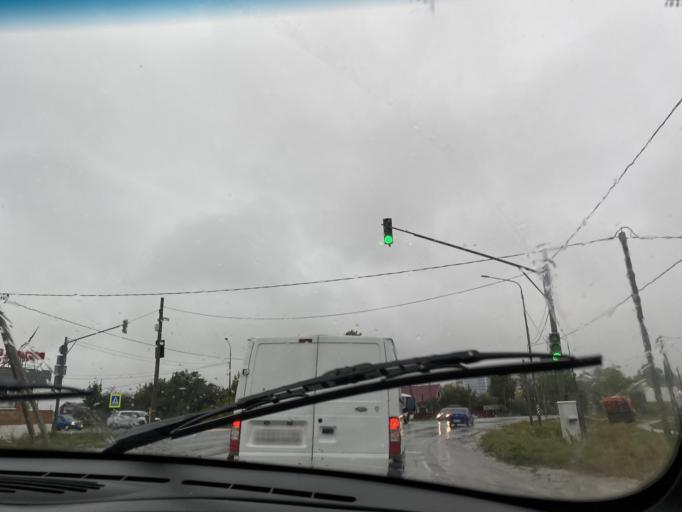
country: RU
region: Rjazan
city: Ryazan'
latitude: 54.5258
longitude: 39.7860
